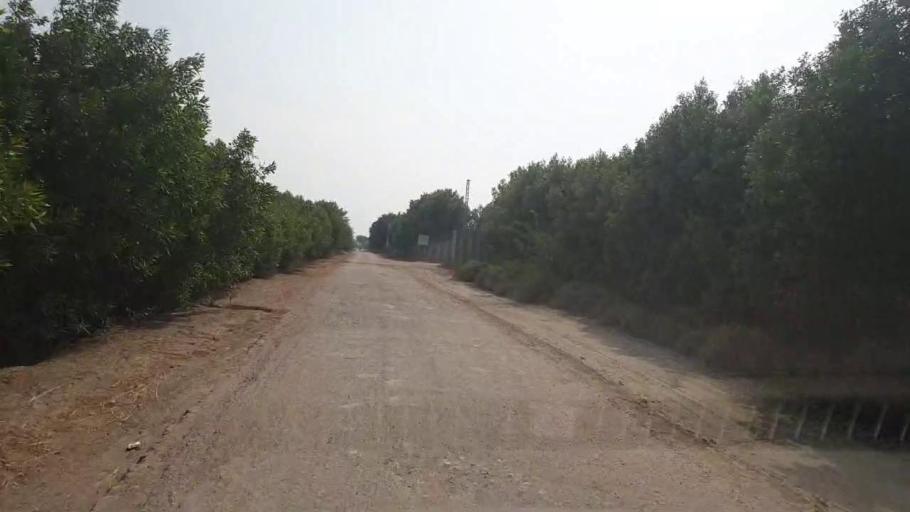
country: PK
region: Sindh
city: Tando Muhammad Khan
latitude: 25.0417
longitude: 68.3912
